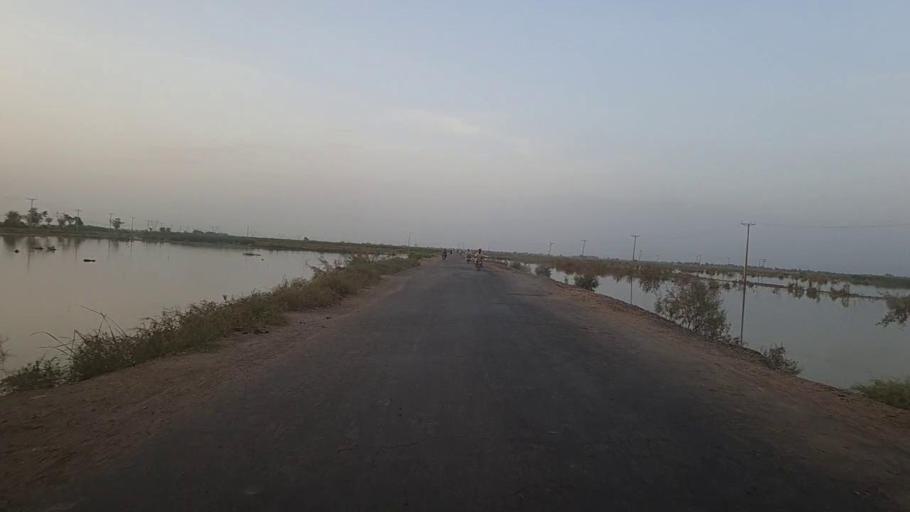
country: PK
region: Sindh
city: Radhan
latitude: 27.1445
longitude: 67.9359
